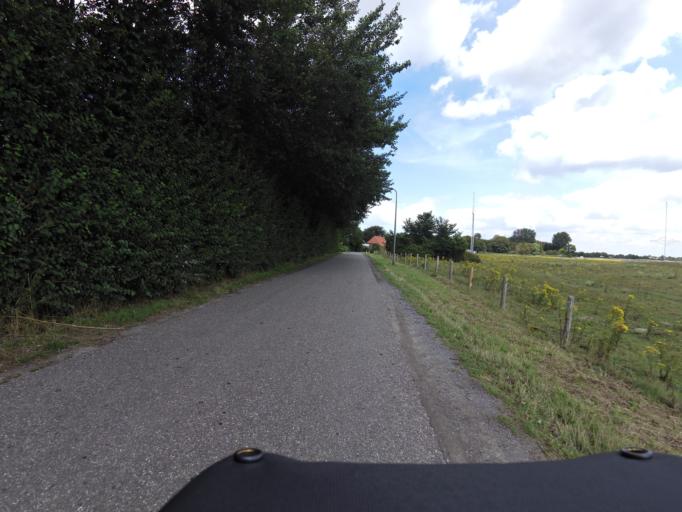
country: NL
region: South Holland
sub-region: Gemeente Goeree-Overflakkee
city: Ouddorp
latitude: 51.8091
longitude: 3.8886
